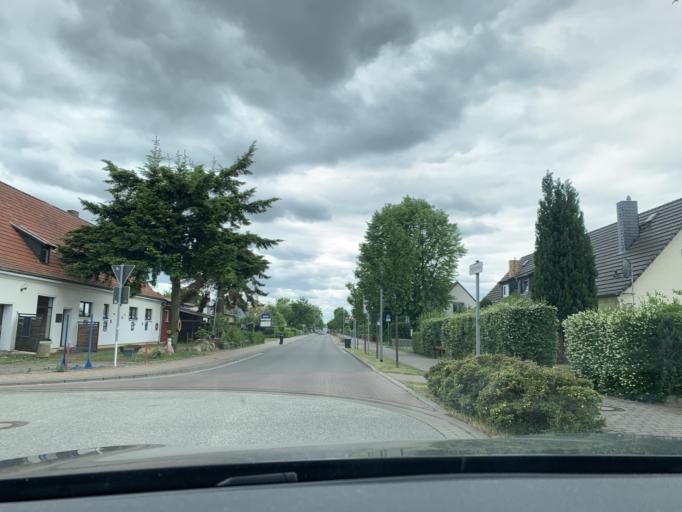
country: DE
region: Mecklenburg-Vorpommern
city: Rechlin
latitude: 53.3324
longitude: 12.7235
